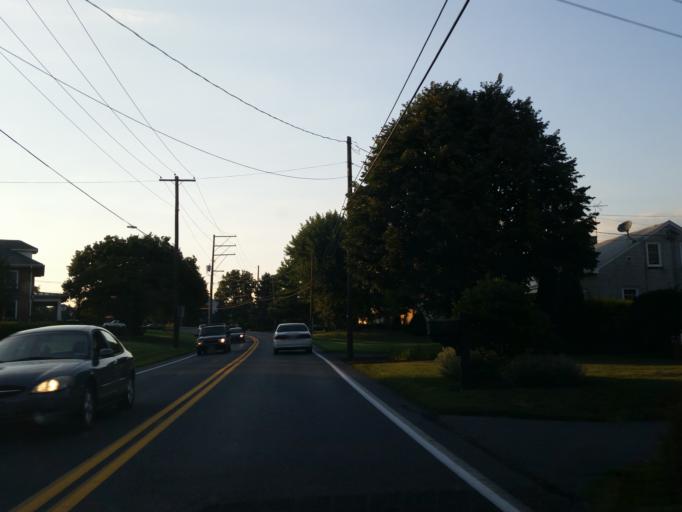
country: US
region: Pennsylvania
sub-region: Lancaster County
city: Reinholds
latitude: 40.2719
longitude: -76.1312
